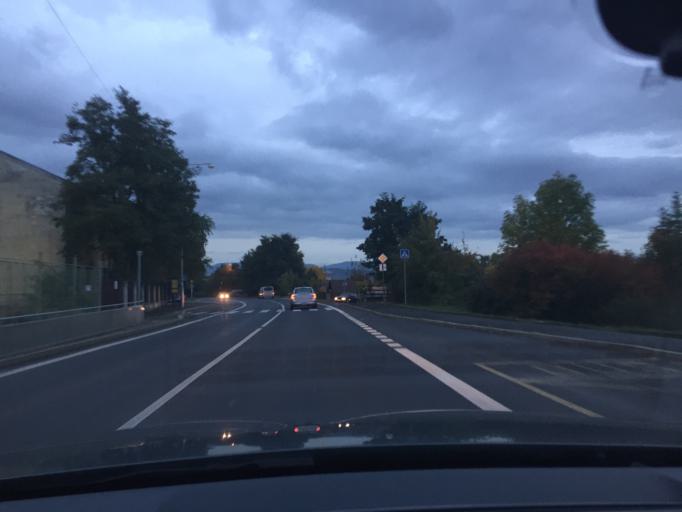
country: CZ
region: Ustecky
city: Dubi
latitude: 50.6669
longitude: 13.7941
